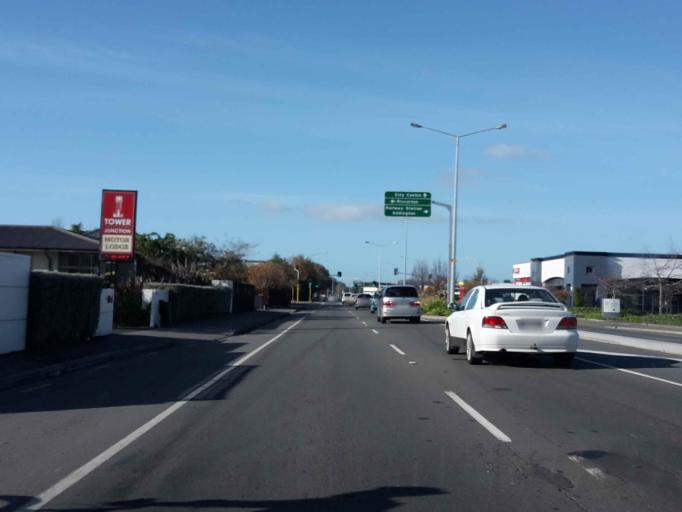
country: NZ
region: Canterbury
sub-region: Christchurch City
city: Christchurch
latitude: -43.5371
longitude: 172.6009
